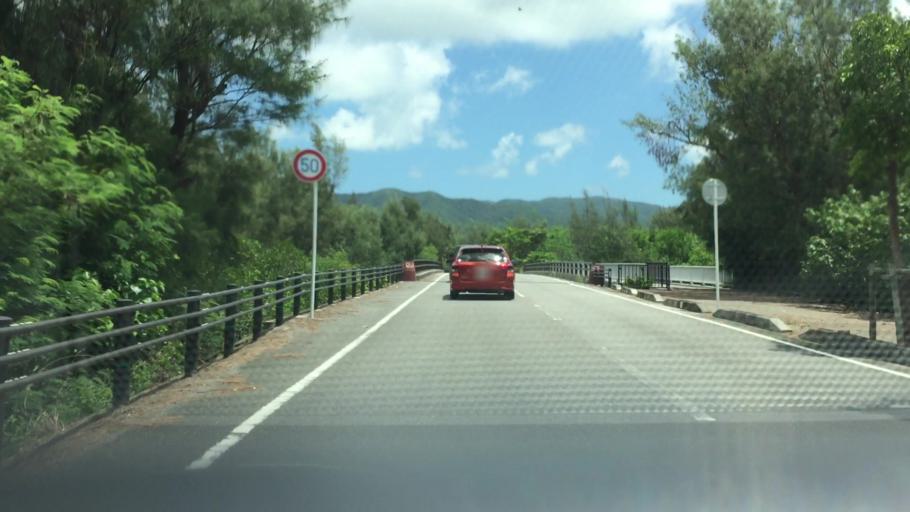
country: JP
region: Okinawa
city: Ishigaki
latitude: 24.3915
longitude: 124.1413
